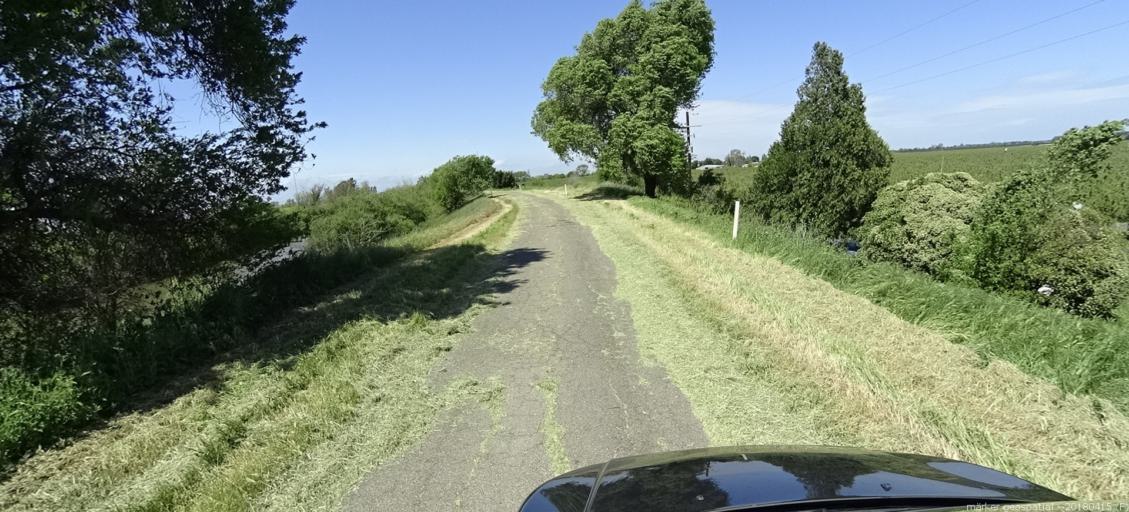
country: US
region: California
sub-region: Sacramento County
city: Walnut Grove
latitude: 38.2816
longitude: -121.6011
